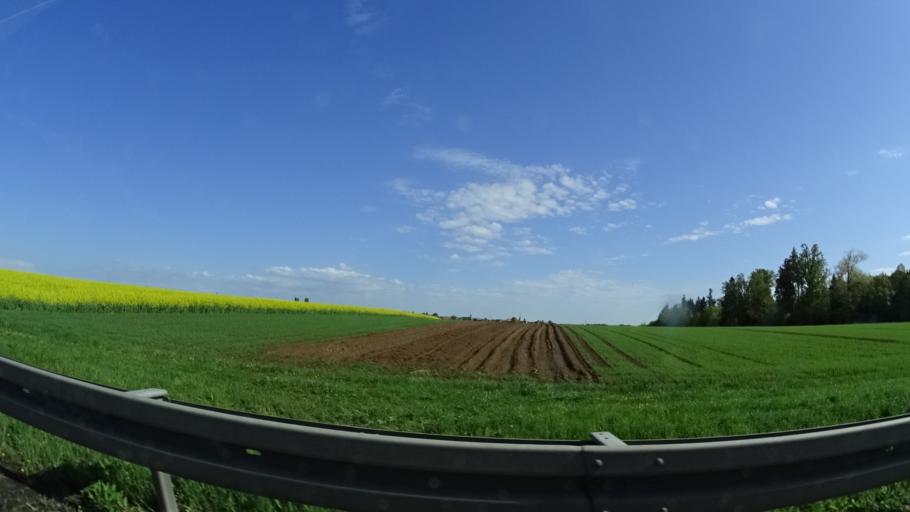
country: DE
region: Baden-Wuerttemberg
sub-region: Regierungsbezirk Stuttgart
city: Motzingen
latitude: 48.5233
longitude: 8.7692
